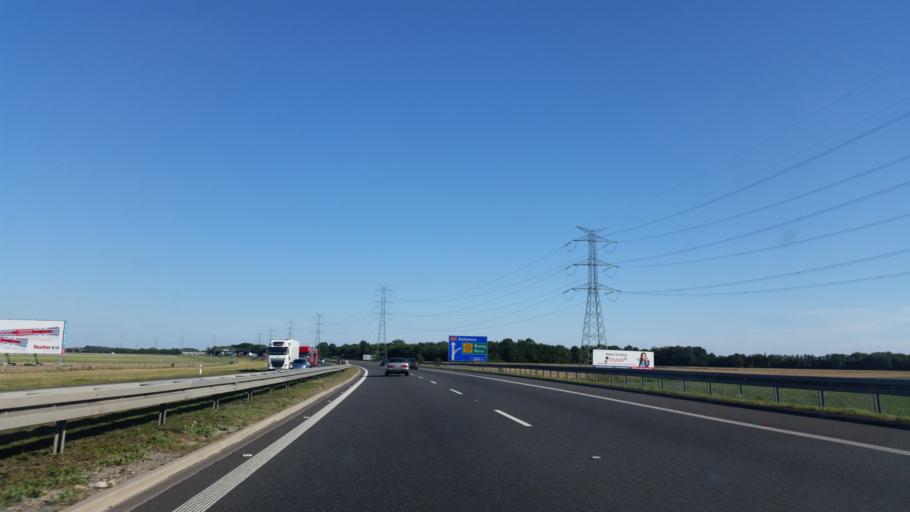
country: PL
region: Opole Voivodeship
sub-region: Powiat brzeski
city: Skarbimierz Osiedle
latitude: 50.7947
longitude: 17.3281
